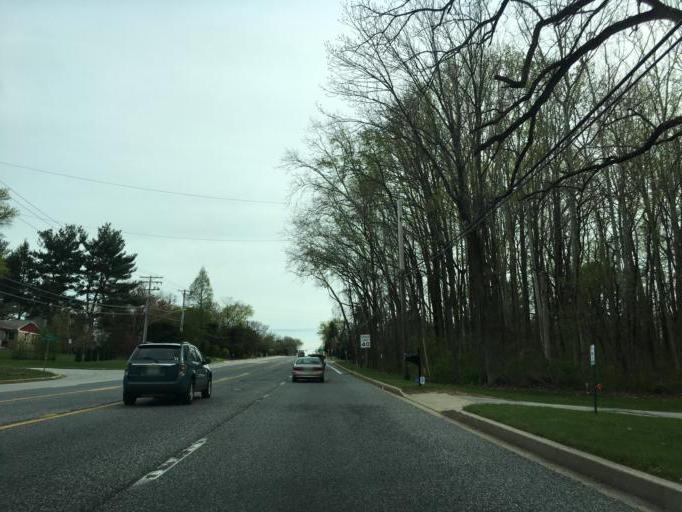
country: US
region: Maryland
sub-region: Baltimore County
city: Hampton
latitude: 39.4194
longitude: -76.5986
